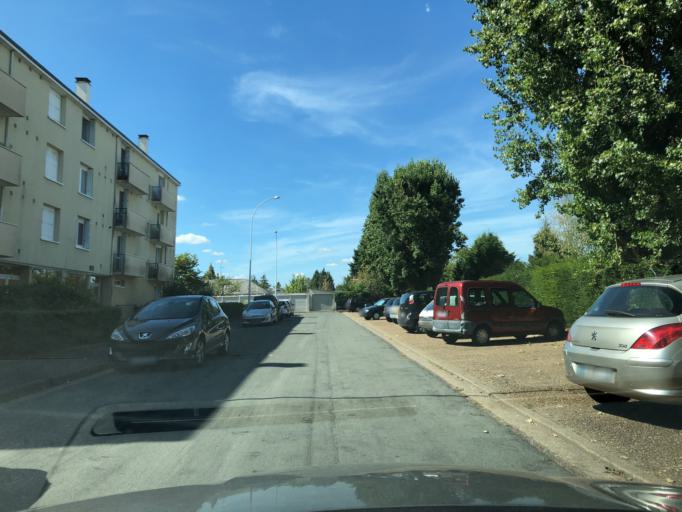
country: FR
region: Centre
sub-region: Departement d'Indre-et-Loire
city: Saint-Cyr-sur-Loire
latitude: 47.4274
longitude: 0.6815
